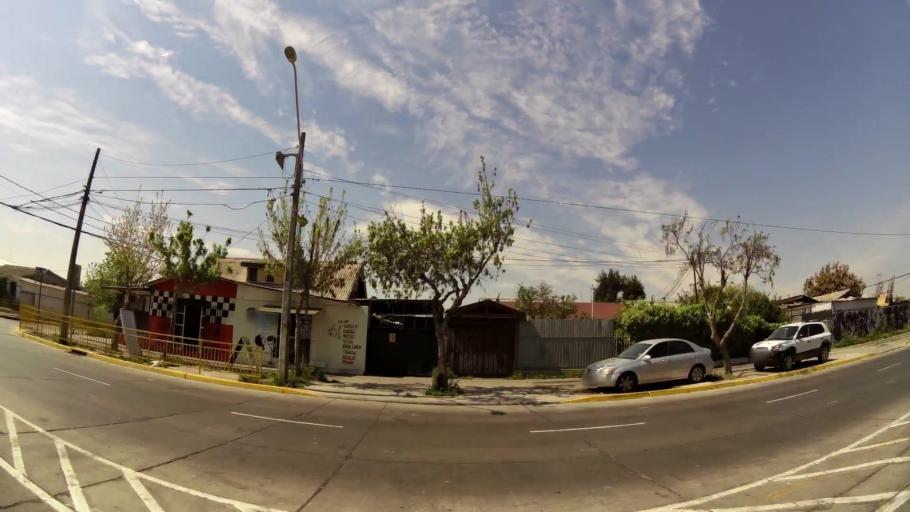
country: CL
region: Santiago Metropolitan
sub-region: Provincia de Santiago
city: La Pintana
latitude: -33.5509
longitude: -70.6679
